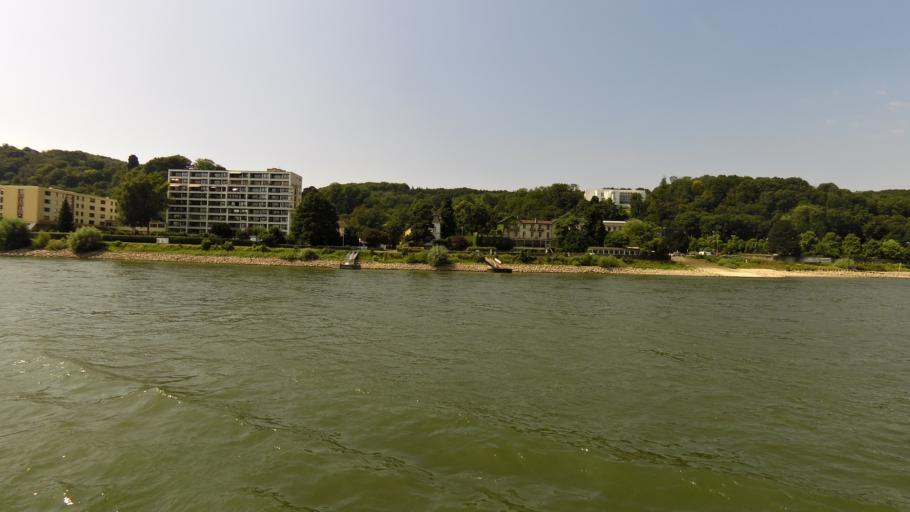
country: DE
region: North Rhine-Westphalia
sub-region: Regierungsbezirk Koln
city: Bad Honnef
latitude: 50.6309
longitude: 7.2115
